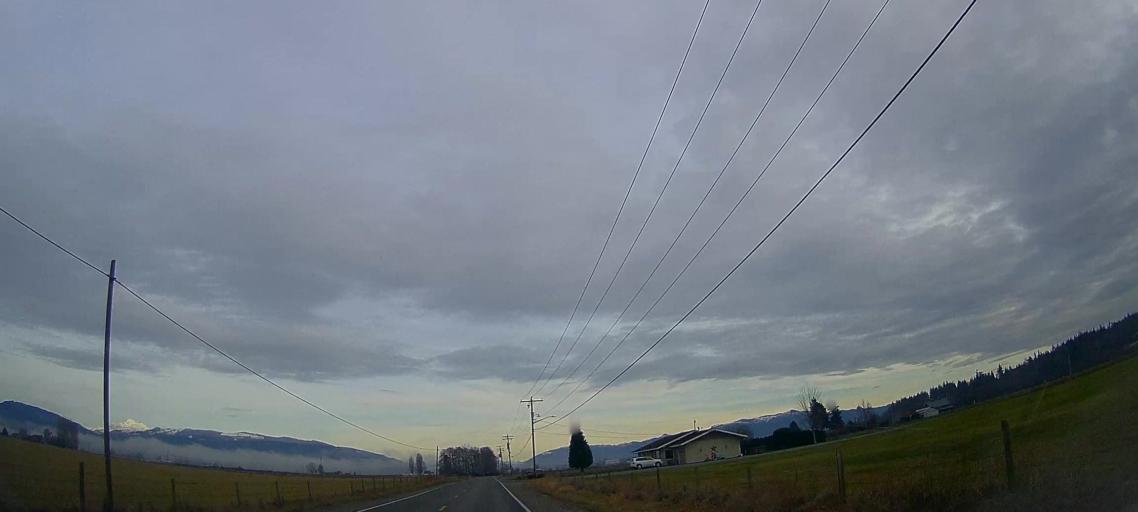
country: US
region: Washington
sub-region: Skagit County
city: Burlington
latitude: 48.5194
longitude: -122.4494
